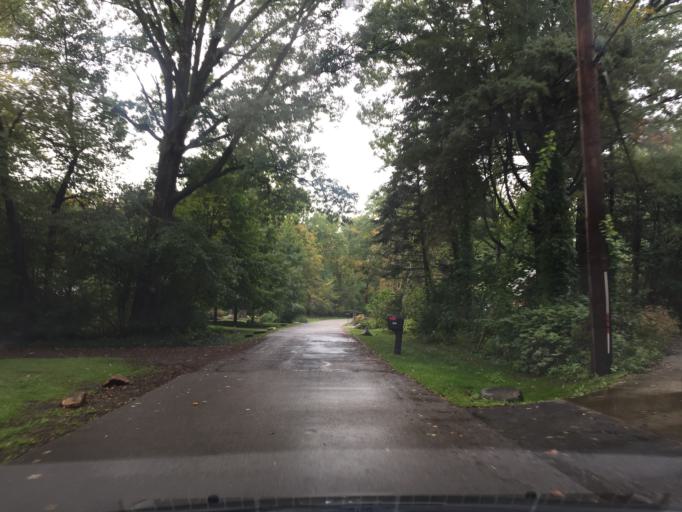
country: US
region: Michigan
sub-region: Oakland County
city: Bingham Farms
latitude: 42.5382
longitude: -83.2688
